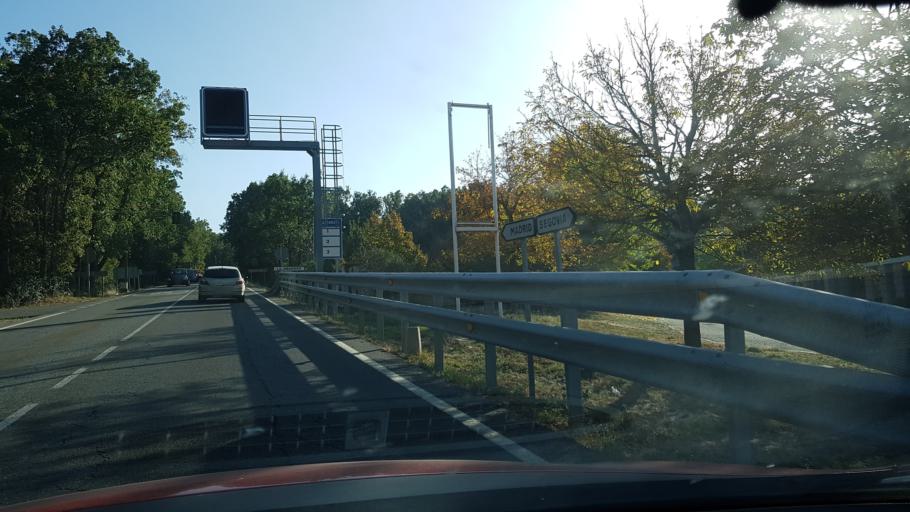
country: ES
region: Castille and Leon
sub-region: Provincia de Segovia
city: San Ildefonso
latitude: 40.8736
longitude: -4.0212
